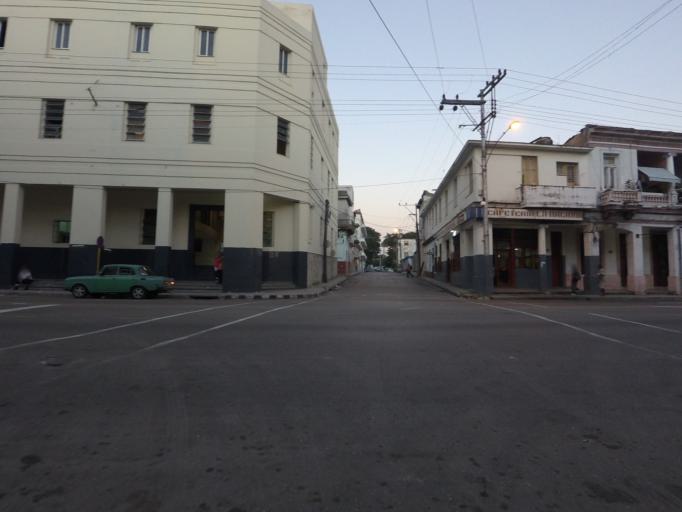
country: CU
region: La Habana
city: Havana
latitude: 23.1267
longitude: -82.3753
